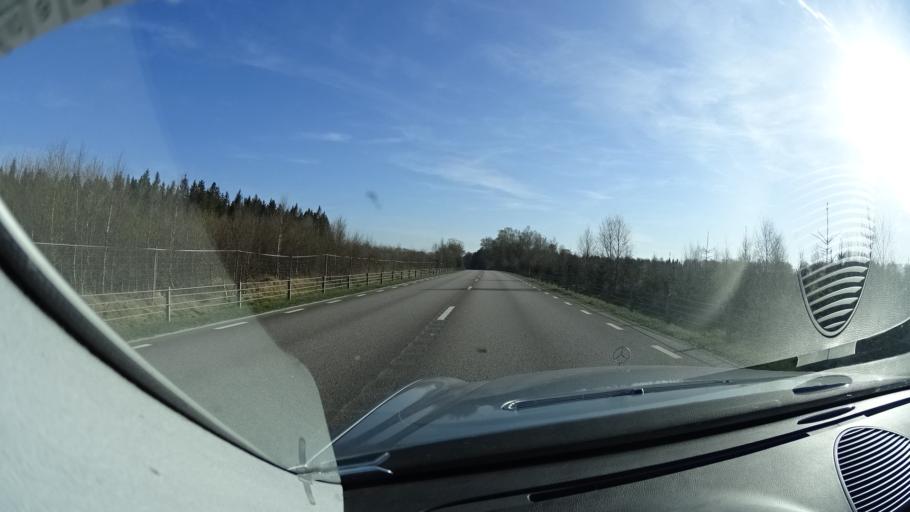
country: SE
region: Skane
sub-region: Bjuvs Kommun
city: Billesholm
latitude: 56.0203
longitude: 12.9613
